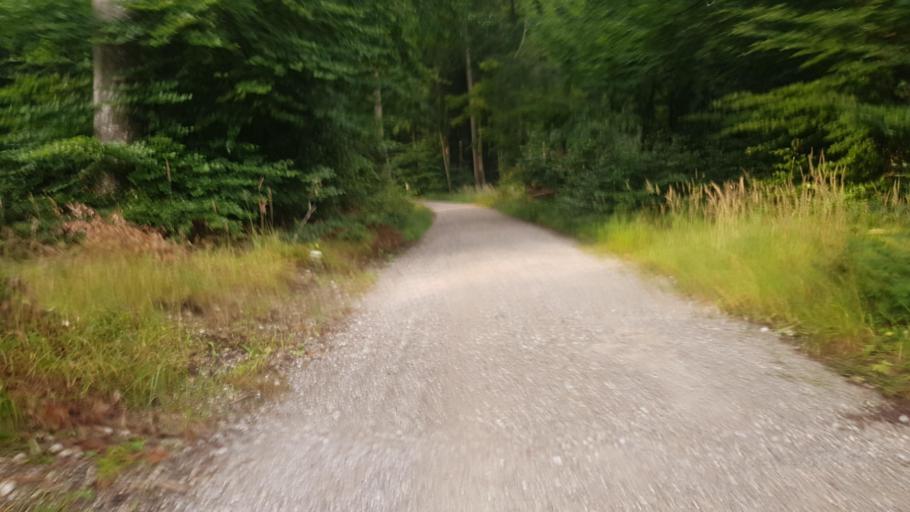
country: DE
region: Bavaria
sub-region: Upper Bavaria
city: Starnberg
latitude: 48.0228
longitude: 11.3412
